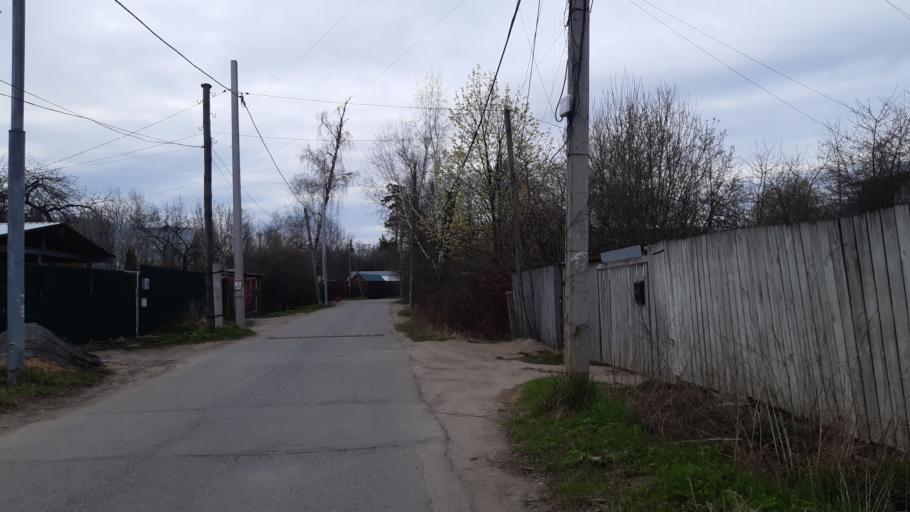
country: RU
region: Moscow
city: Severnyy
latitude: 55.9270
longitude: 37.5288
